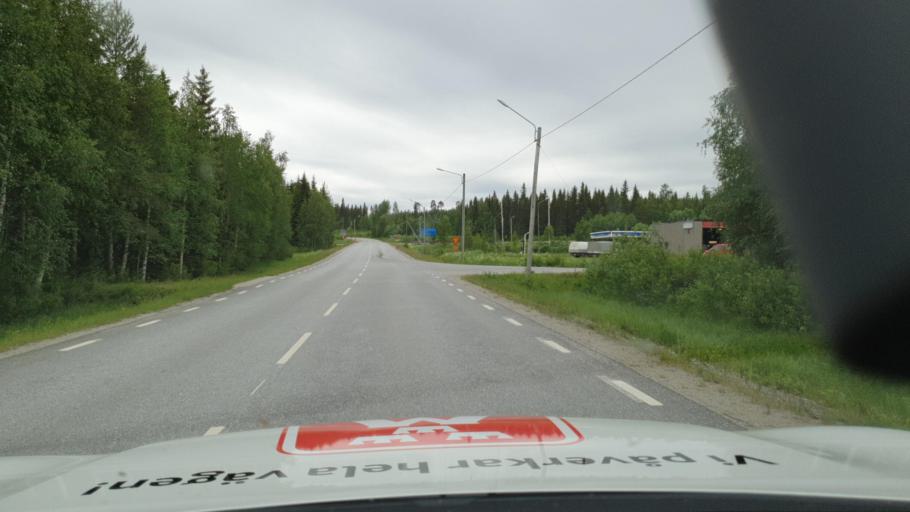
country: SE
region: Vaesterbotten
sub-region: Lycksele Kommun
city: Lycksele
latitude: 64.0713
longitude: 18.3965
